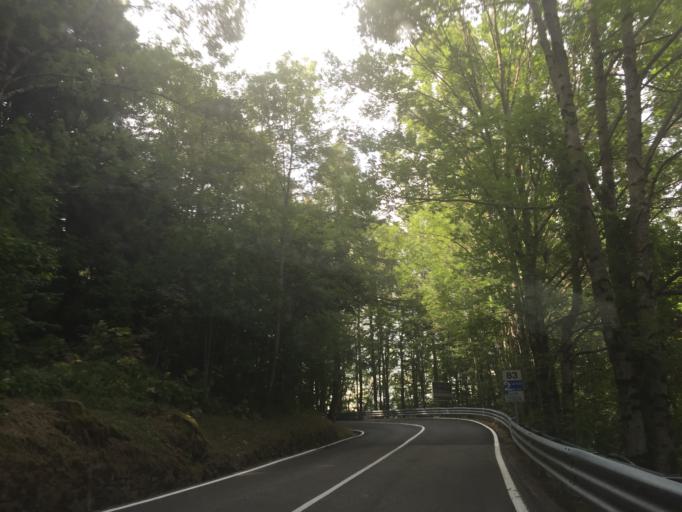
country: IT
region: Tuscany
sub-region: Provincia di Pistoia
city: Cutigliano
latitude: 44.1234
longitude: 10.7149
